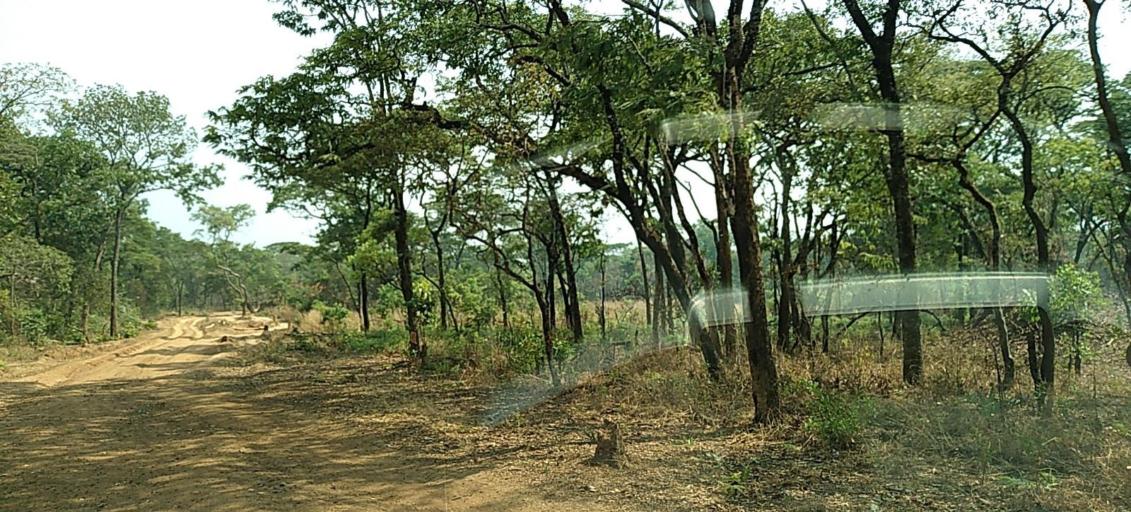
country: ZM
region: North-Western
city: Kansanshi
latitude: -12.0766
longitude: 26.8878
